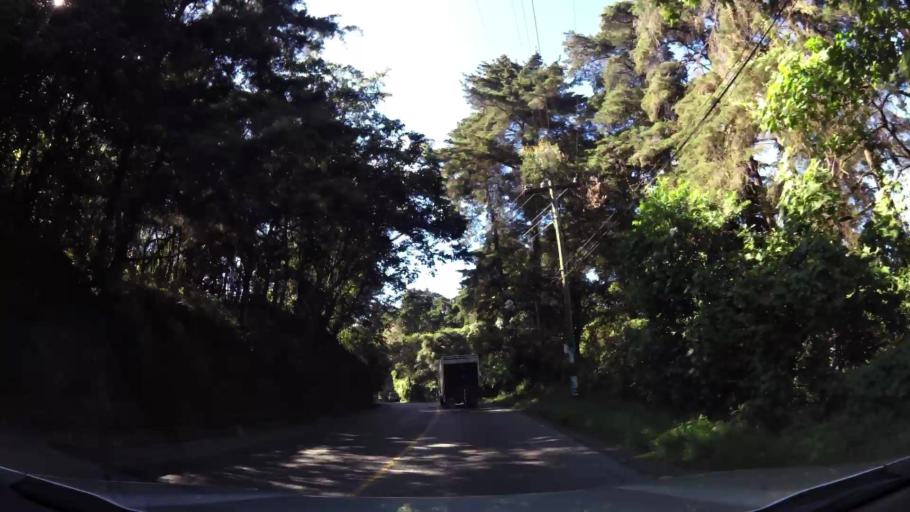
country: GT
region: Sacatepequez
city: Santa Lucia Milpas Altas
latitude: 14.5813
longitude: -90.6541
